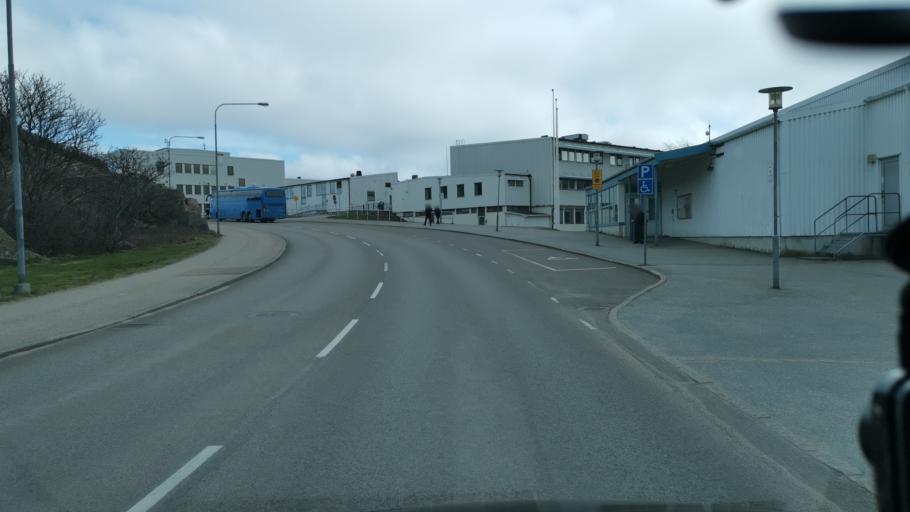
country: SE
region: Vaestra Goetaland
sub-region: Lysekils Kommun
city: Lysekil
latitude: 58.2794
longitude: 11.4361
